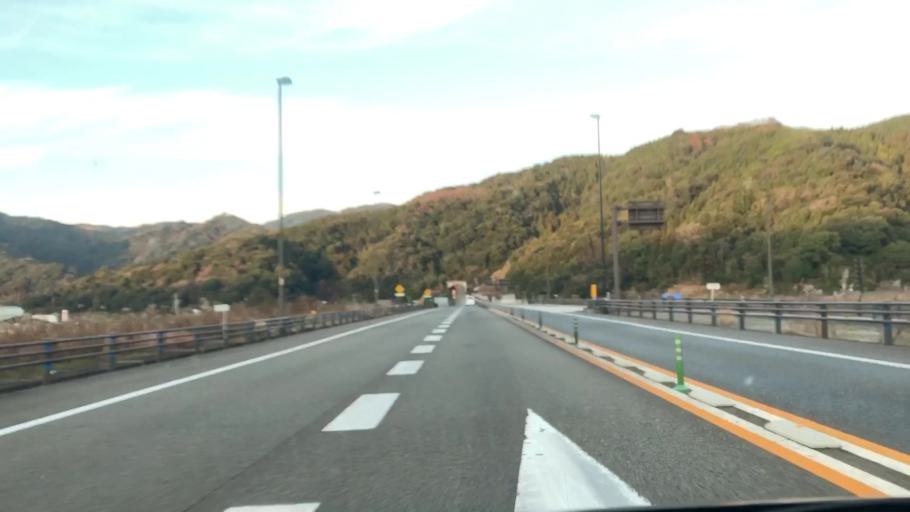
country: JP
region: Kumamoto
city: Minamata
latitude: 32.2986
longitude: 130.5092
